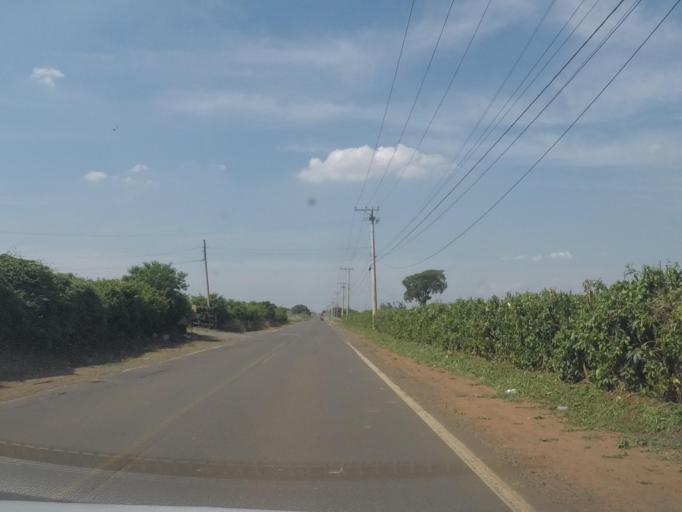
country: BR
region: Sao Paulo
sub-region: Sumare
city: Sumare
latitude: -22.8772
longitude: -47.3006
